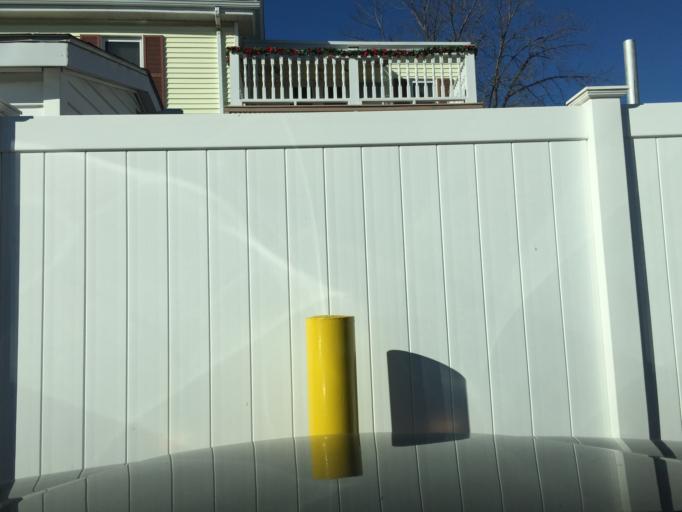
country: US
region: Massachusetts
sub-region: Middlesex County
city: Cambridge
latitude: 42.3863
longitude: -71.1146
